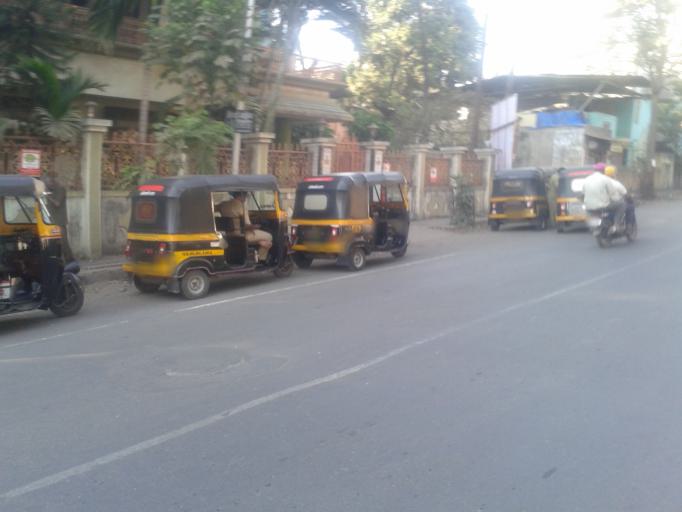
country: IN
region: Maharashtra
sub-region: Thane
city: Dombivli
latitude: 19.2056
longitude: 73.0890
